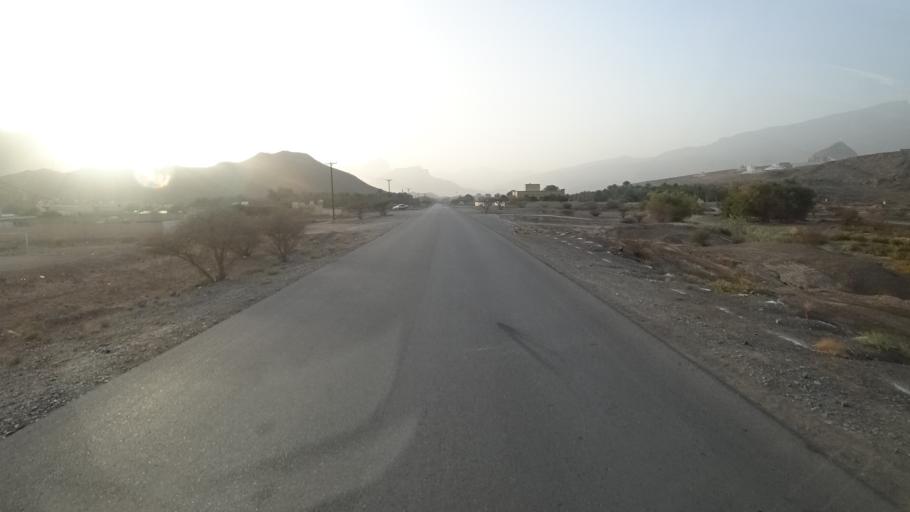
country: OM
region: Muhafazat ad Dakhiliyah
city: Bahla'
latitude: 23.0817
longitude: 57.3261
